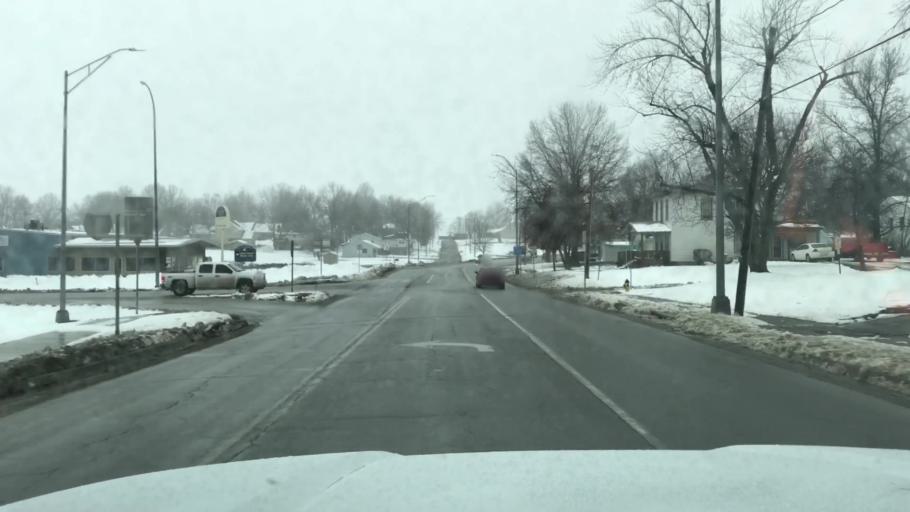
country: US
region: Missouri
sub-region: Clinton County
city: Cameron
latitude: 39.7323
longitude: -94.2360
